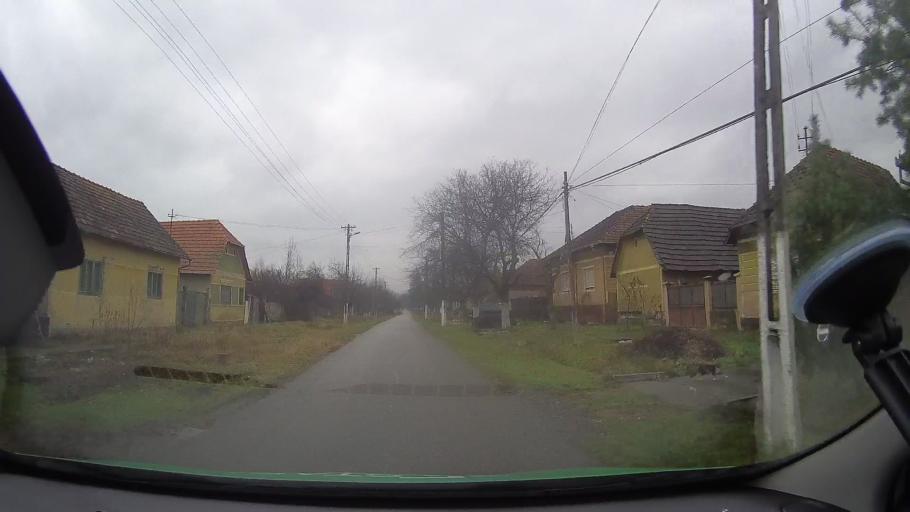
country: RO
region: Arad
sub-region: Comuna Brazii
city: Brazii
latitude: 46.2387
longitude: 22.3330
